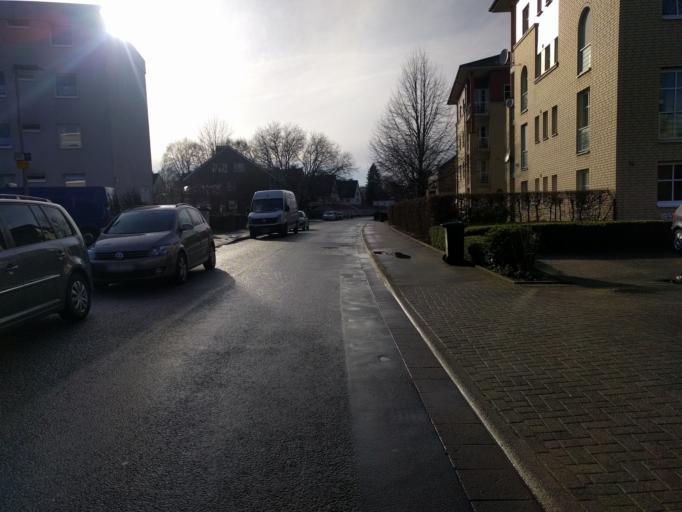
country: DE
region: North Rhine-Westphalia
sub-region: Regierungsbezirk Detmold
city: Bielefeld
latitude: 52.0484
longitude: 8.5197
